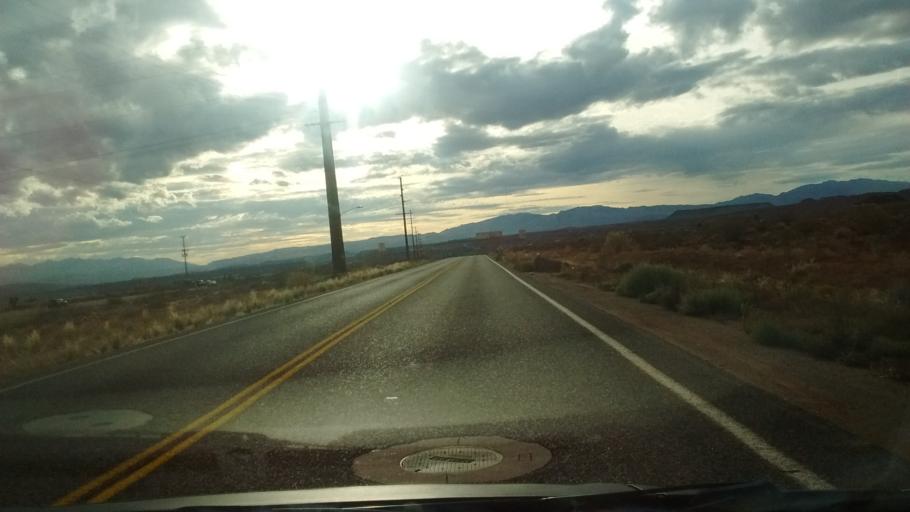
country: US
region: Utah
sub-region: Washington County
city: Washington
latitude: 37.1452
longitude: -113.4960
